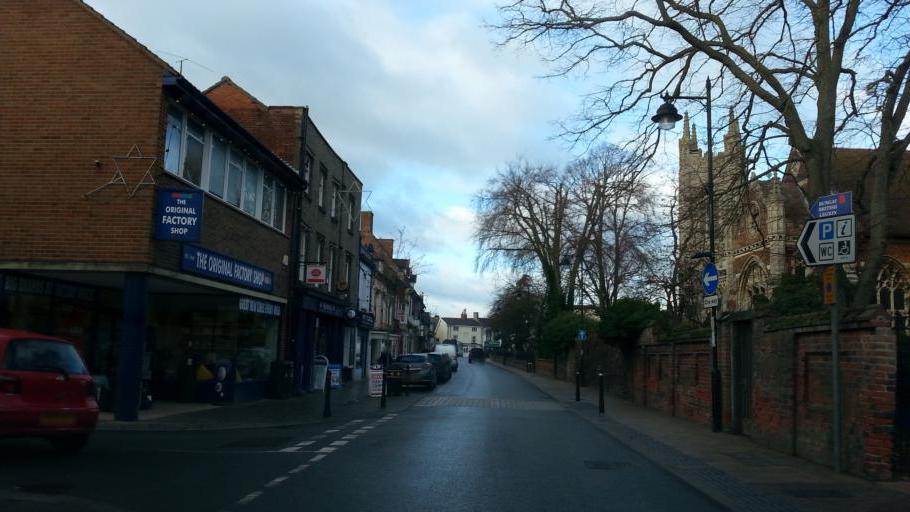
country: GB
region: England
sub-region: Suffolk
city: Bungay
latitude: 52.4546
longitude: 1.4381
